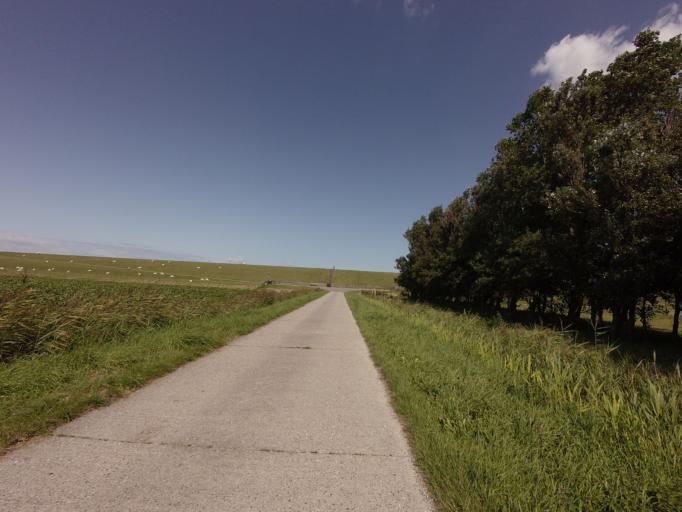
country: NL
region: Friesland
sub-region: Gemeente Ferwerderadiel
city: Hallum
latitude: 53.3233
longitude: 5.7221
